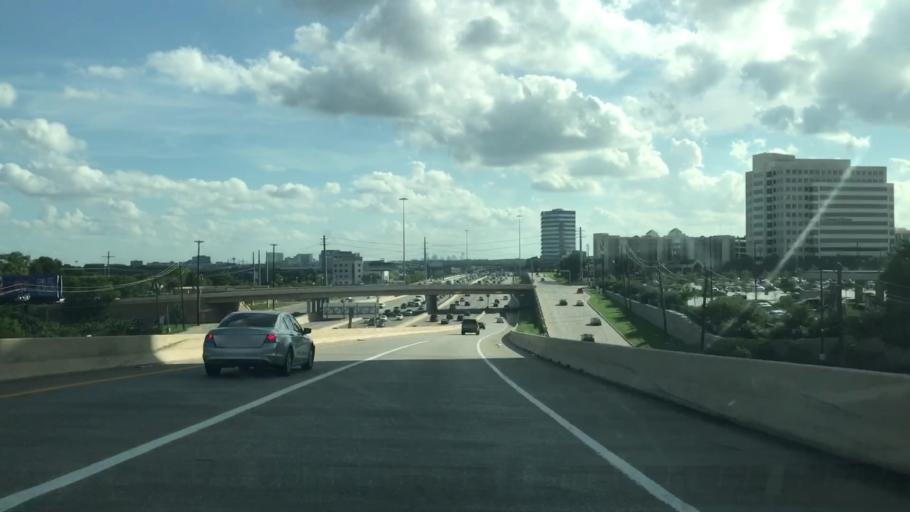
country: US
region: Texas
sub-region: Dallas County
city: Richardson
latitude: 32.9209
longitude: -96.7658
